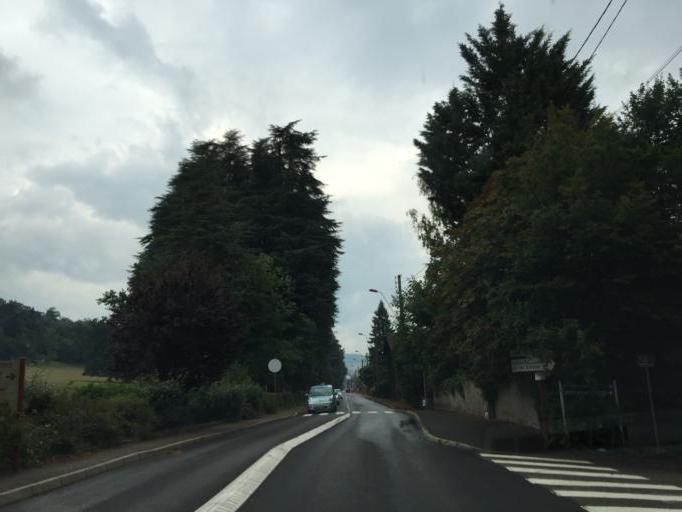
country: FR
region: Rhone-Alpes
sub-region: Departement de la Loire
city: La Talaudiere
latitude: 45.4877
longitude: 4.4361
